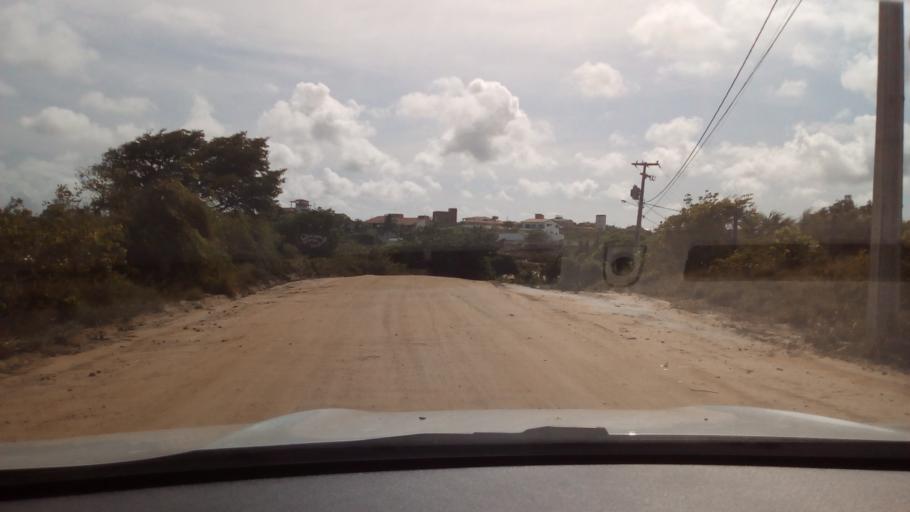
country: BR
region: Paraiba
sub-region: Conde
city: Conde
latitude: -7.3053
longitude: -34.8048
